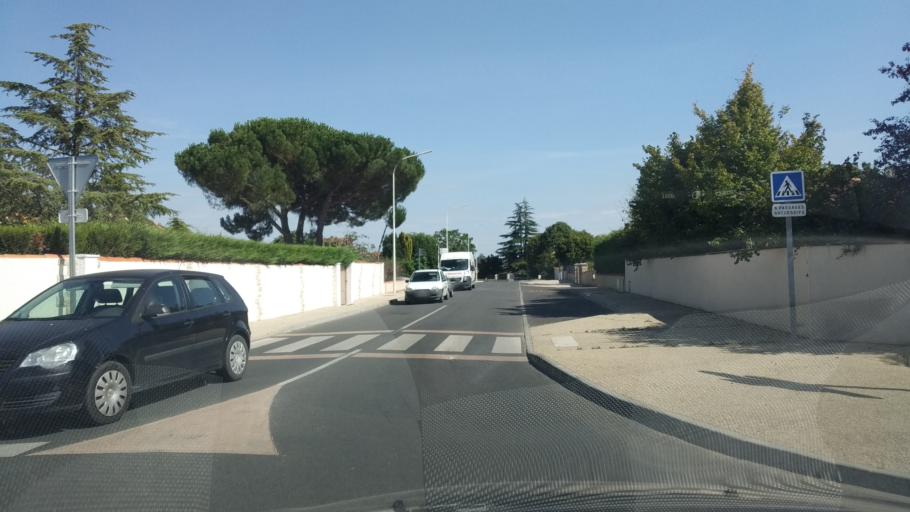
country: FR
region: Poitou-Charentes
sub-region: Departement de la Vienne
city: Cisse
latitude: 46.6484
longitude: 0.2250
